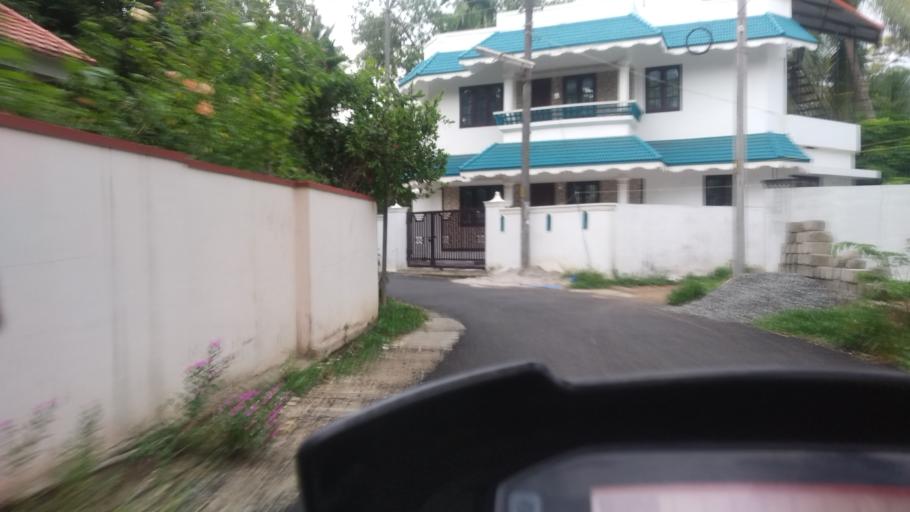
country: IN
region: Kerala
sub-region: Ernakulam
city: Elur
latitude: 10.0661
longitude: 76.2152
